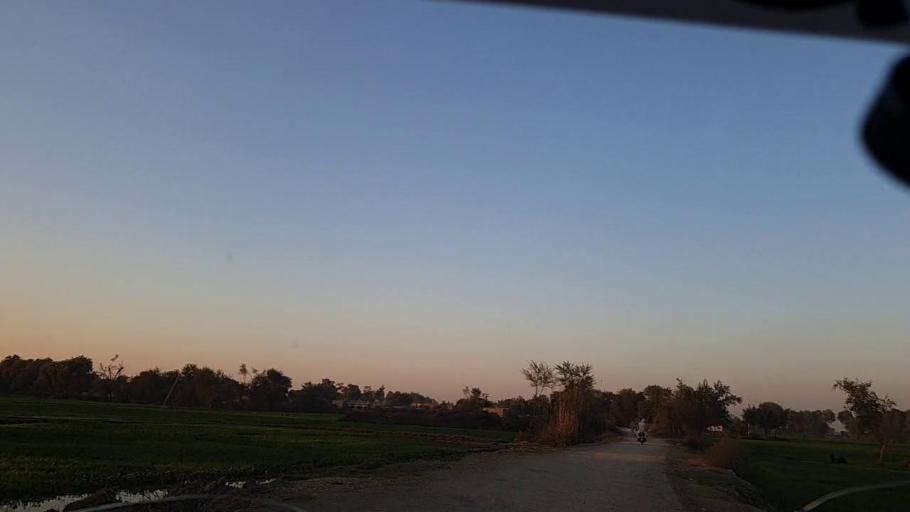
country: PK
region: Sindh
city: Adilpur
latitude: 27.8392
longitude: 69.2983
